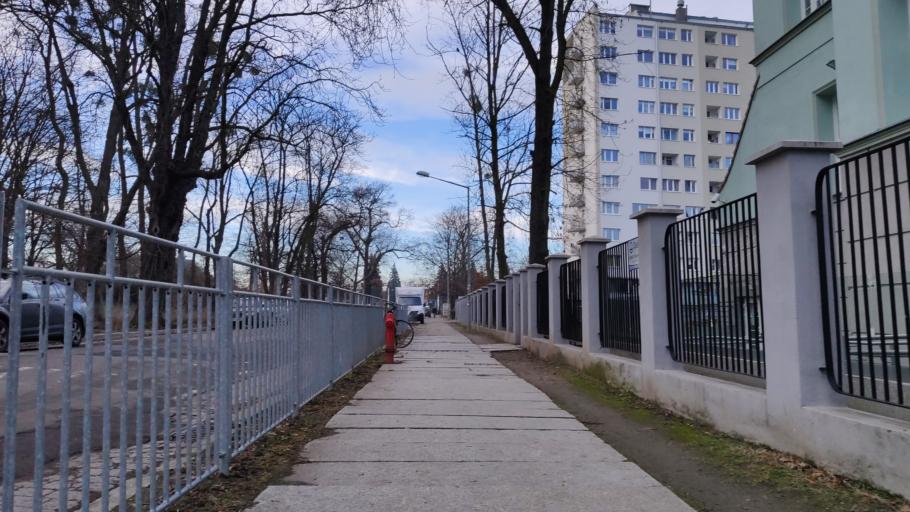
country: PL
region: Lower Silesian Voivodeship
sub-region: Powiat wroclawski
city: Wroclaw
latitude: 51.0792
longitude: 17.0101
